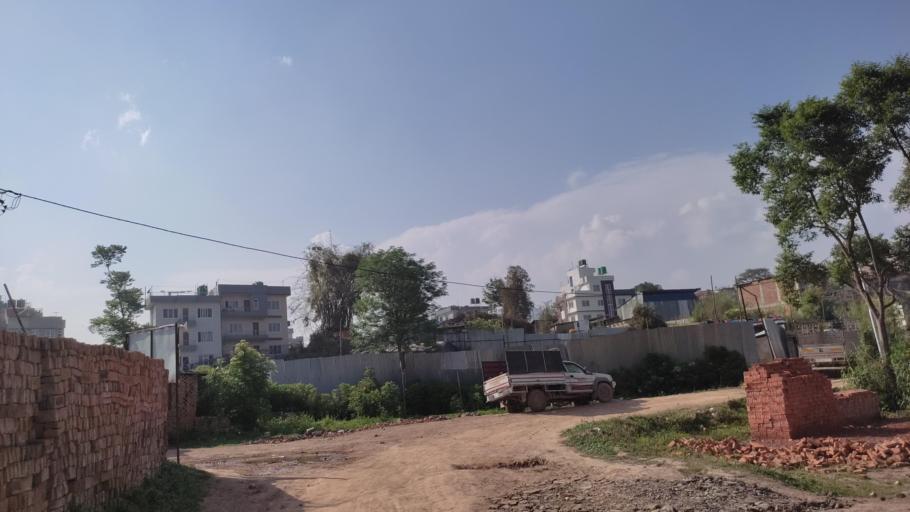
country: NP
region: Central Region
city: Kirtipur
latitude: 27.6800
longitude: 85.2626
